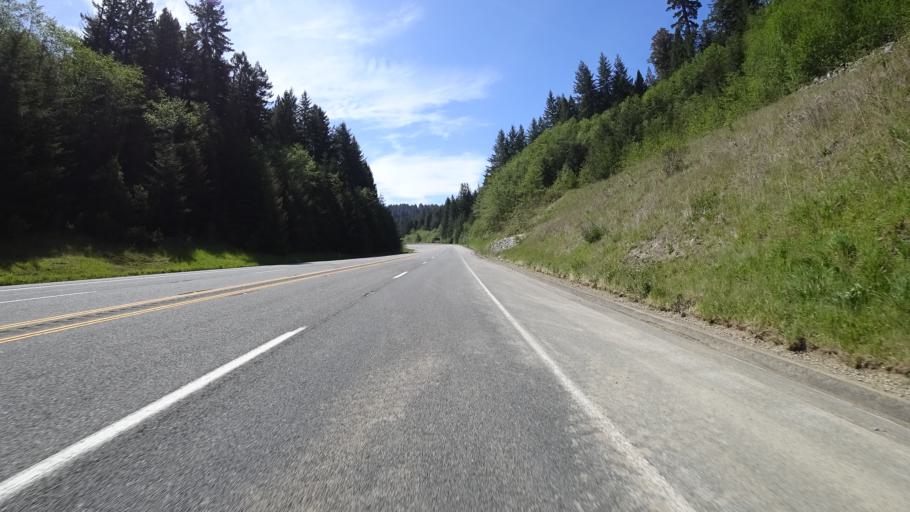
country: US
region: California
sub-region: Del Norte County
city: Bertsch-Oceanview
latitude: 41.4575
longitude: -124.0313
